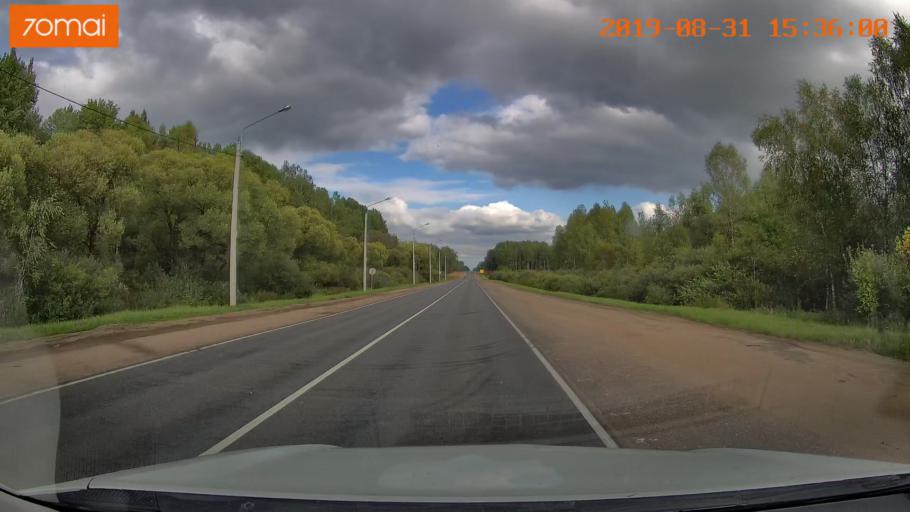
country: RU
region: Kaluga
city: Mosal'sk
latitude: 54.6083
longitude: 34.7483
